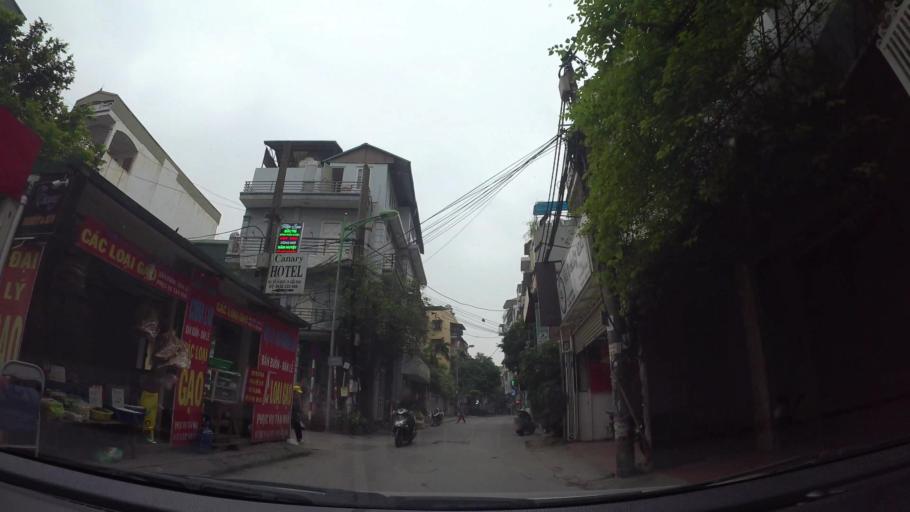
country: VN
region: Ha Noi
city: Cau Giay
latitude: 21.0338
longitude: 105.8172
